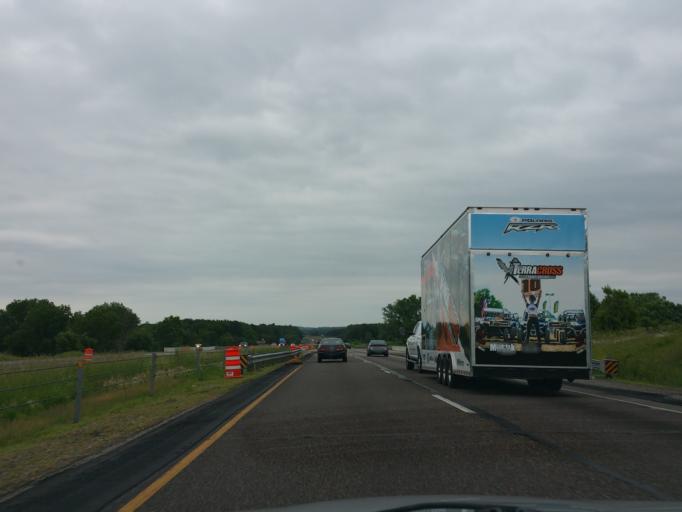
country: US
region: Wisconsin
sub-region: Dunn County
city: Colfax
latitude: 44.8568
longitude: -91.6595
